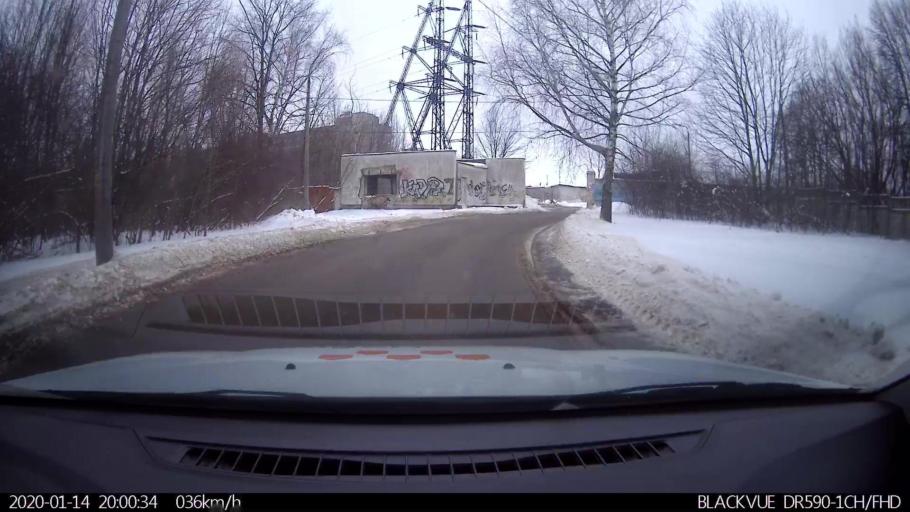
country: RU
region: Nizjnij Novgorod
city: Nizhniy Novgorod
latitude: 56.2375
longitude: 43.9402
